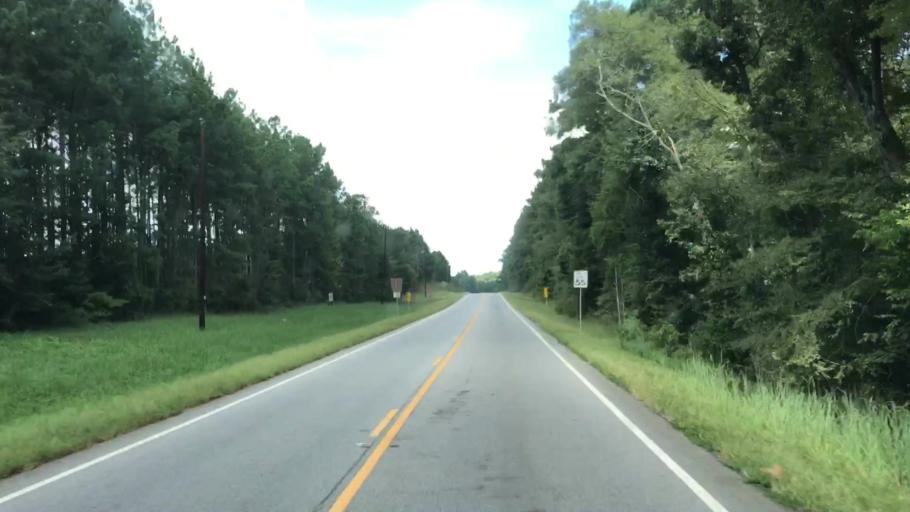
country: US
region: Georgia
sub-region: Greene County
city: Greensboro
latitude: 33.7033
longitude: -83.2851
